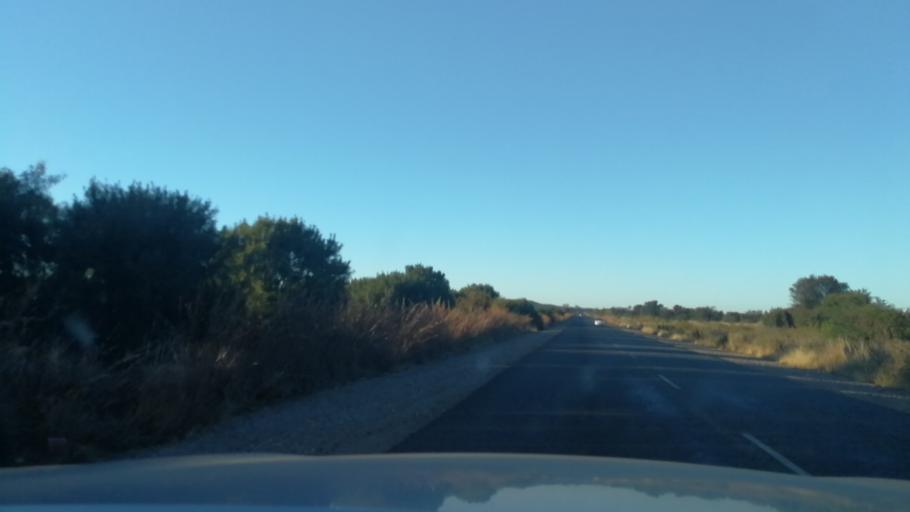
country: ZA
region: North-West
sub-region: Bojanala Platinum District Municipality
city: Koster
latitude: -25.7110
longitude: 26.7399
